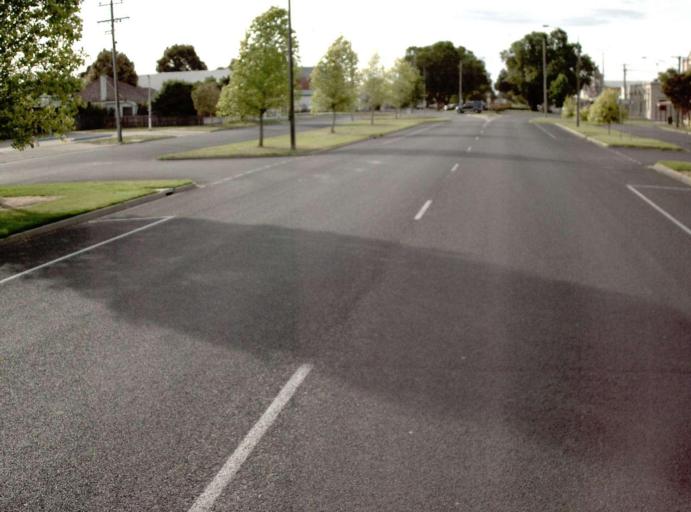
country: AU
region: Victoria
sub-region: Wellington
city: Sale
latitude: -37.9689
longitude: 146.9798
